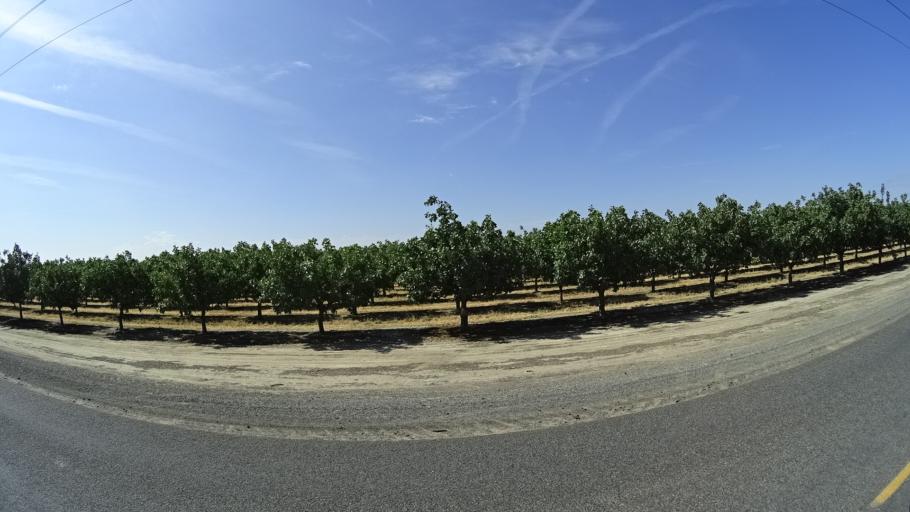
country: US
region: California
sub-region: Kings County
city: Armona
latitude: 36.2548
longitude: -119.6833
